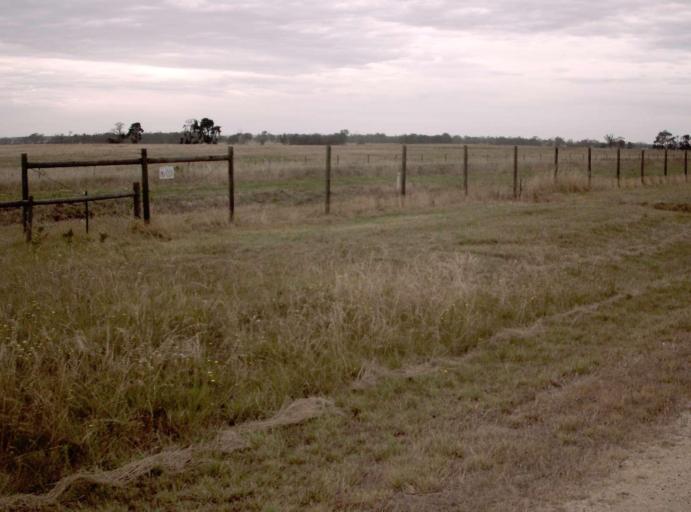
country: AU
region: Victoria
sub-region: Wellington
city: Sale
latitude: -38.1771
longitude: 147.2123
